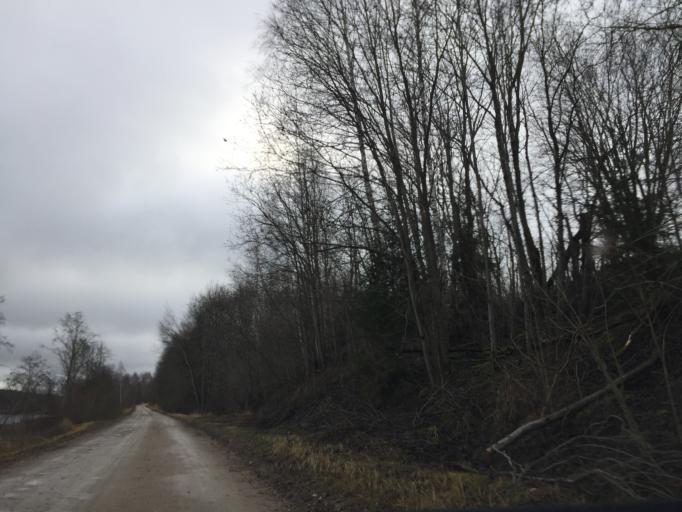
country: LV
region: Broceni
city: Broceni
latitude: 56.6624
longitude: 22.5528
